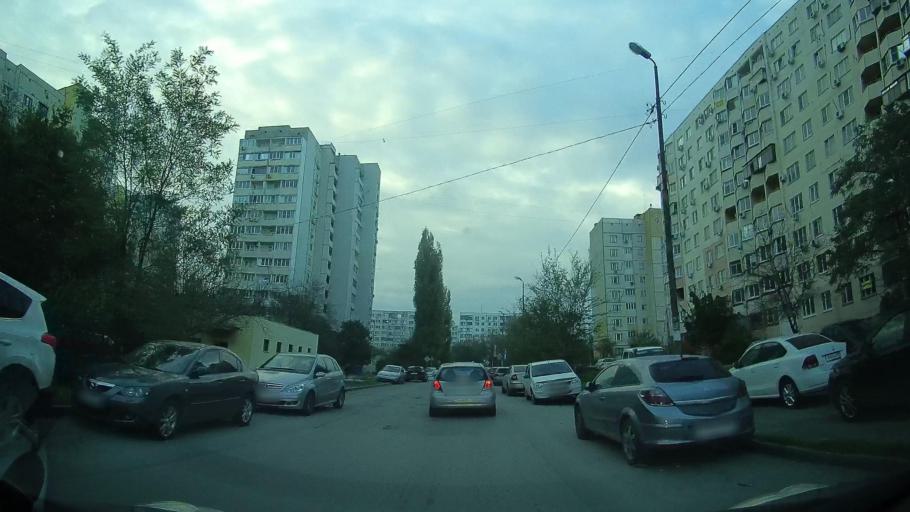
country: RU
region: Rostov
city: Severnyy
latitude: 47.2591
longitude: 39.6439
